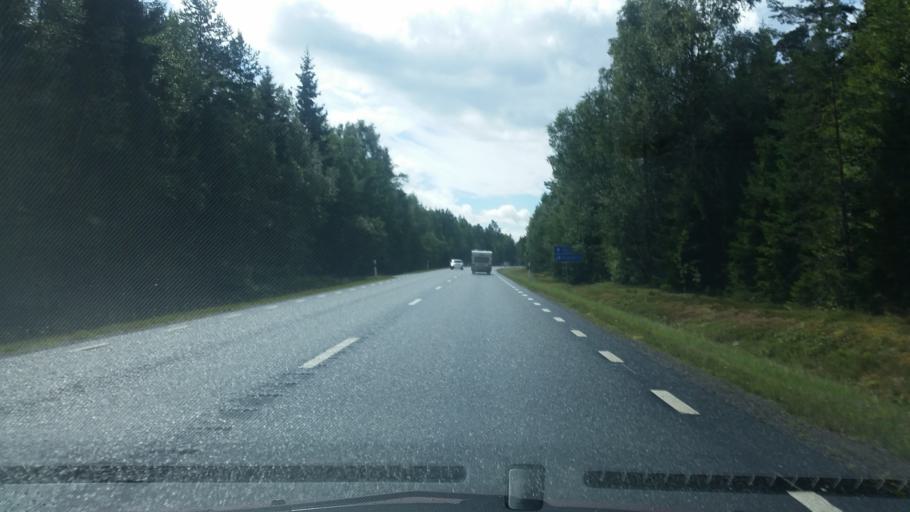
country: SE
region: Joenkoeping
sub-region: Gislaveds Kommun
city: Gislaved
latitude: 57.3907
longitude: 13.5892
